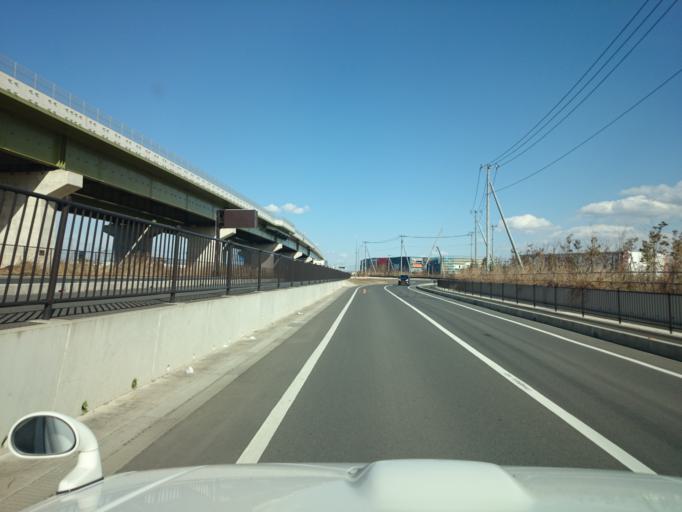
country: JP
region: Saitama
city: Satte
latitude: 36.0640
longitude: 139.7380
